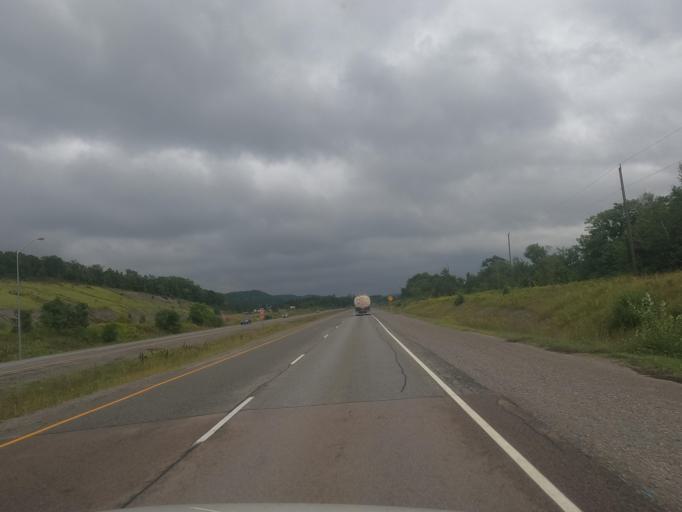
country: CA
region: Ontario
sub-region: Algoma
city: Sault Ste. Marie
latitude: 46.5496
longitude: -84.1498
